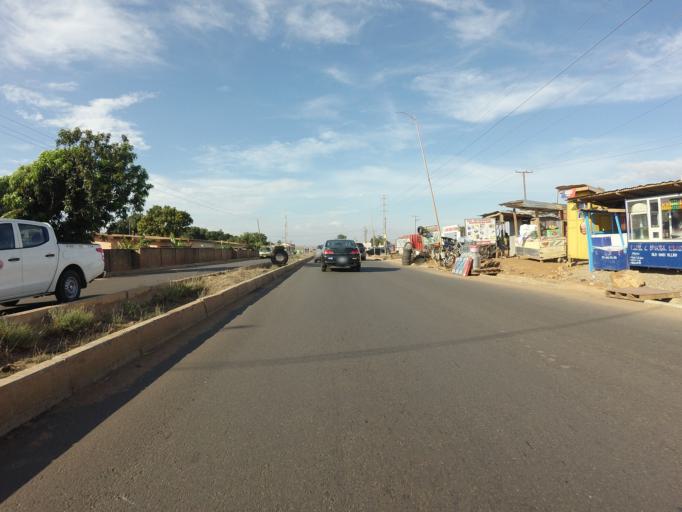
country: GH
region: Greater Accra
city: Nungua
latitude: 5.6402
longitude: -0.0615
